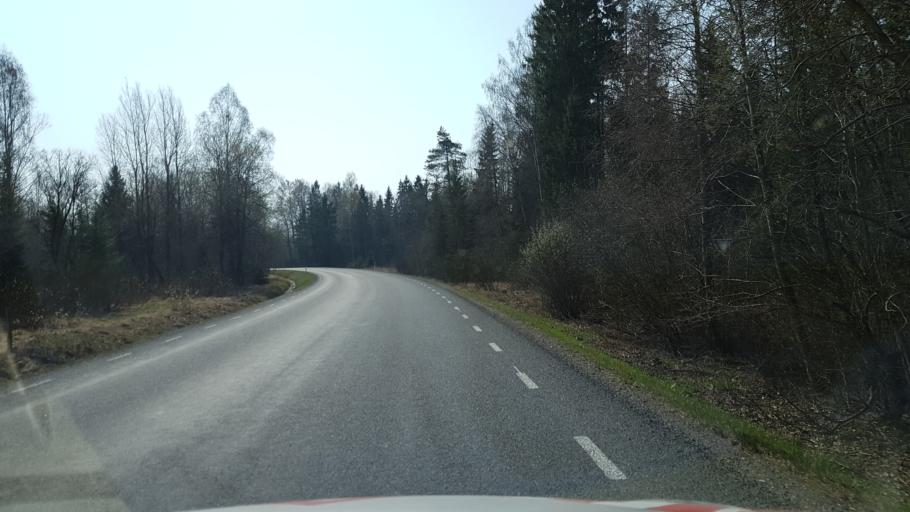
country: EE
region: Raplamaa
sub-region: Kehtna vald
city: Kehtna
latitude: 59.0310
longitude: 24.9223
